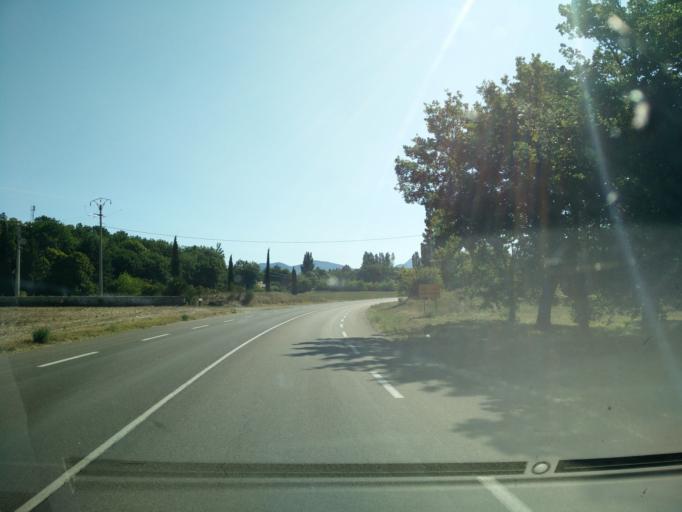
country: FR
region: Rhone-Alpes
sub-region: Departement de la Drome
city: La Begude-de-Mazenc
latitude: 44.5324
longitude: 4.9987
